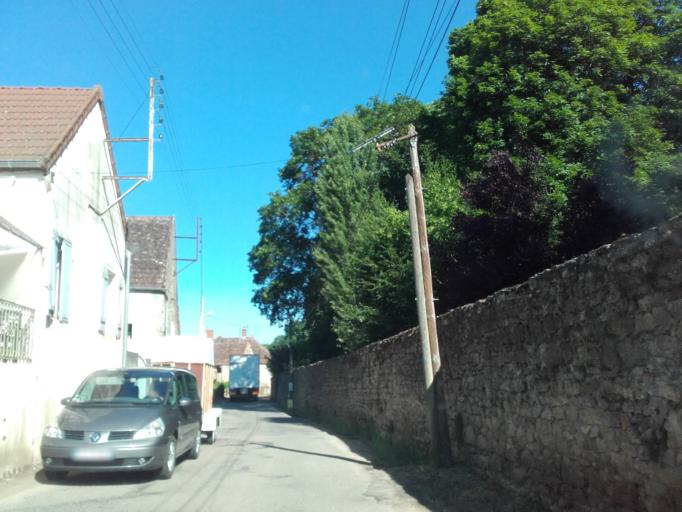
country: FR
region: Bourgogne
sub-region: Departement de Saone-et-Loire
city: Saint-Leger-sur-Dheune
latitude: 46.8684
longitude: 4.6258
